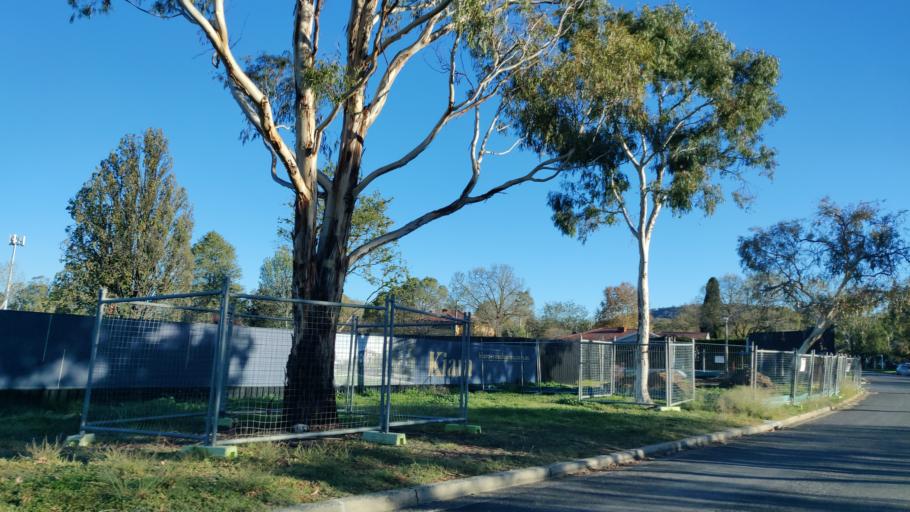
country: AU
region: Australian Capital Territory
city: Forrest
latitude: -35.3318
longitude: 149.1447
